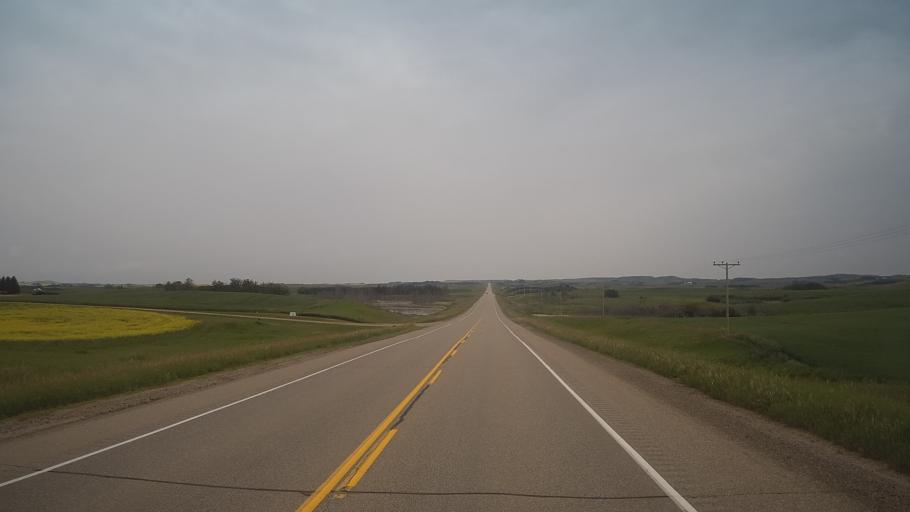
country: CA
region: Saskatchewan
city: Biggar
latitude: 52.0565
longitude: -107.7989
